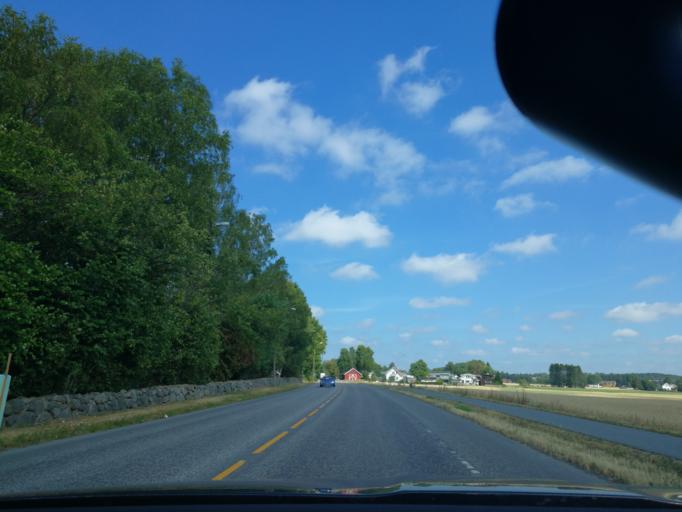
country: NO
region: Vestfold
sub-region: Sandefjord
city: Sandefjord
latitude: 59.1564
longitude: 10.1995
